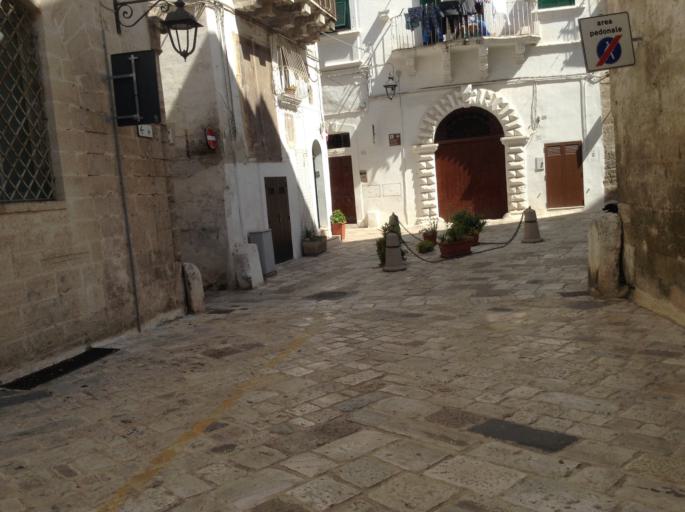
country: IT
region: Apulia
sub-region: Provincia di Bari
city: Monopoli
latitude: 40.9517
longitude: 17.3023
